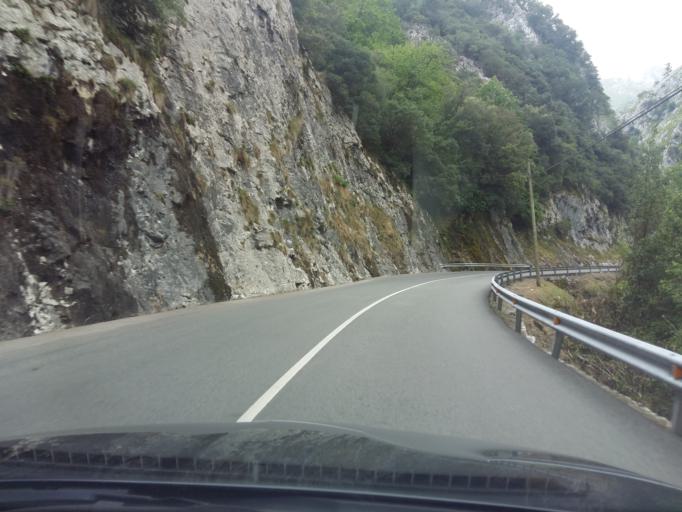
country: ES
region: Cantabria
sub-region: Provincia de Cantabria
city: Tresviso
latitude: 43.3095
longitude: -4.6080
